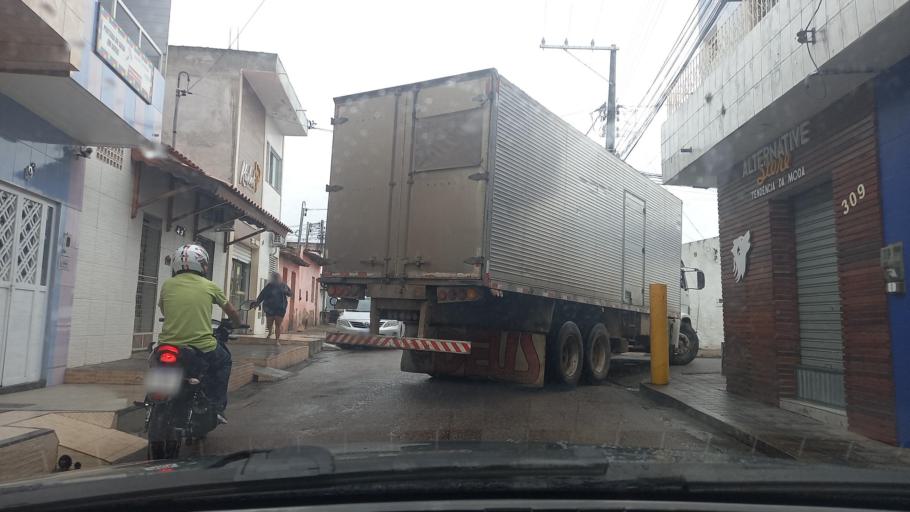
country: BR
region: Bahia
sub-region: Paulo Afonso
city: Paulo Afonso
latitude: -9.4062
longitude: -38.2210
